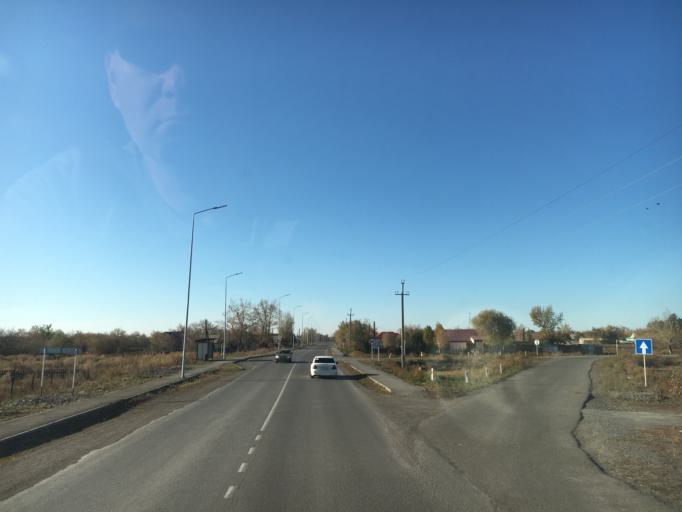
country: KZ
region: Qaraghandy
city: Tokarevka
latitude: 50.1351
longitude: 73.1830
